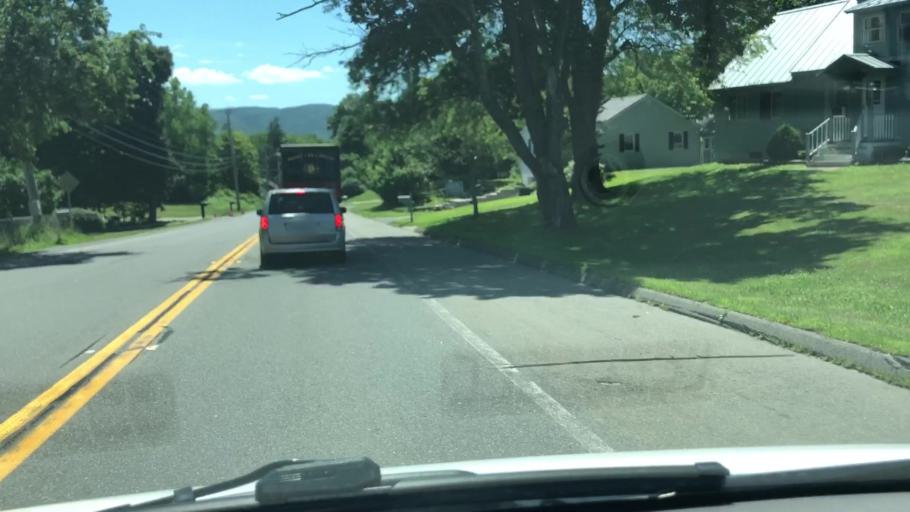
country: US
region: Massachusetts
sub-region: Berkshire County
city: Adams
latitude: 42.5845
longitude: -73.1469
